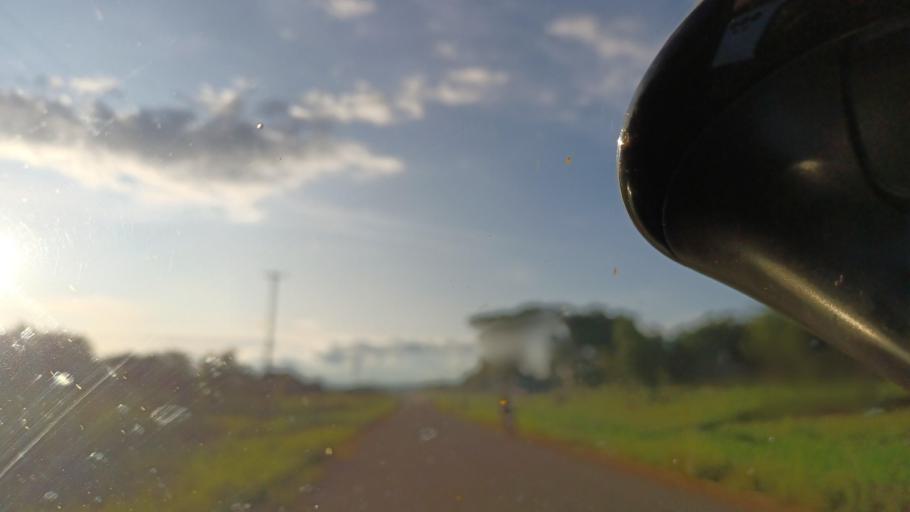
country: ZM
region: North-Western
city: Kasempa
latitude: -13.4654
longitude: 25.8571
